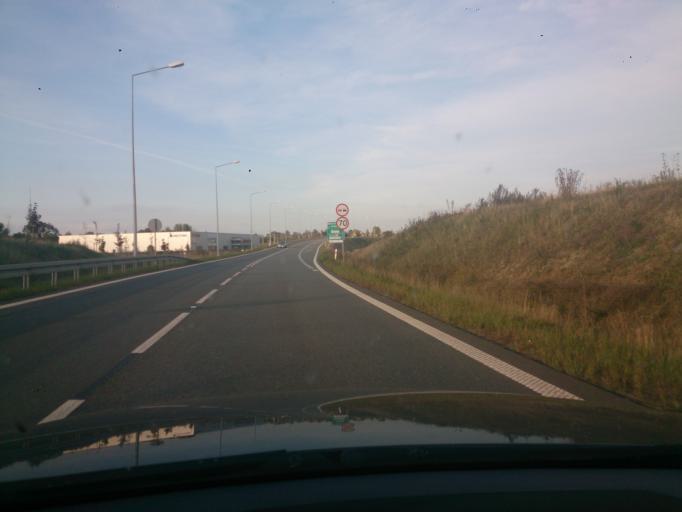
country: PL
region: Kujawsko-Pomorskie
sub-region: Grudziadz
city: Grudziadz
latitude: 53.4369
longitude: 18.7112
